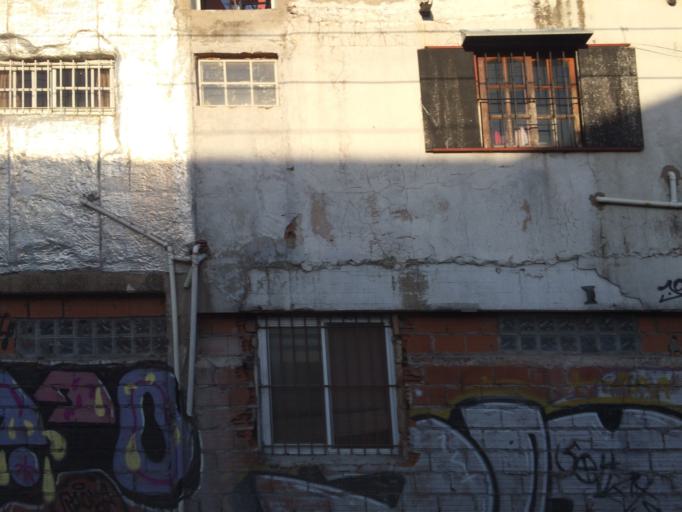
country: AR
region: Buenos Aires
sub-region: Partido de Lomas de Zamora
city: Lomas de Zamora
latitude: -34.7467
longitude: -58.3956
